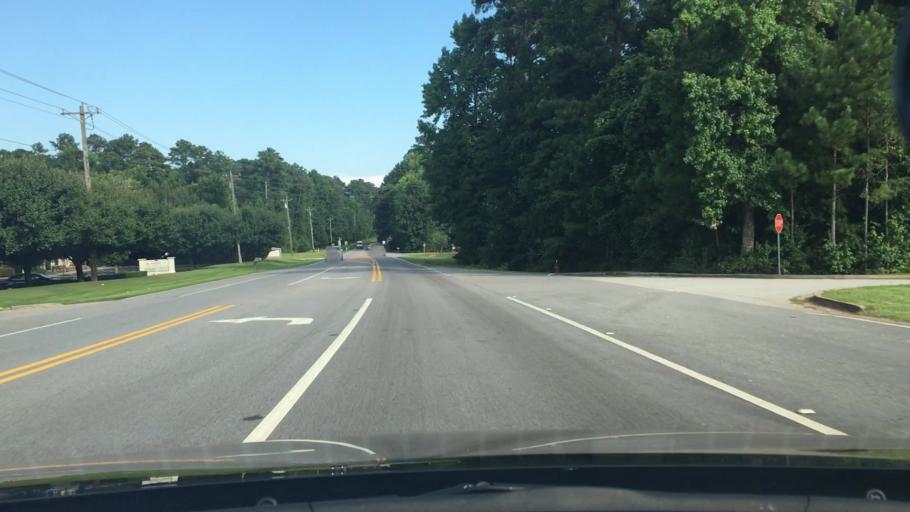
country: US
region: Georgia
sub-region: Coweta County
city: East Newnan
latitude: 33.3426
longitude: -84.6882
